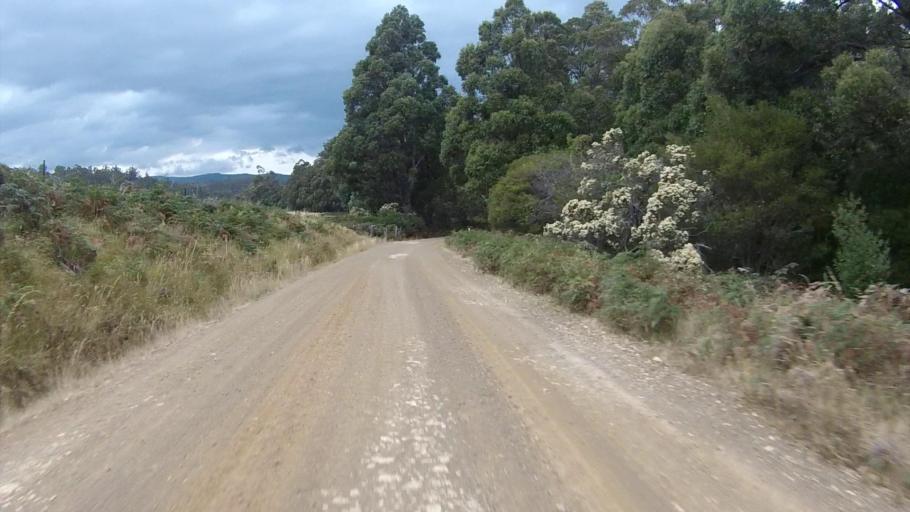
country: AU
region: Tasmania
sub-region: Huon Valley
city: Huonville
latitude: -42.9586
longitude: 147.0501
